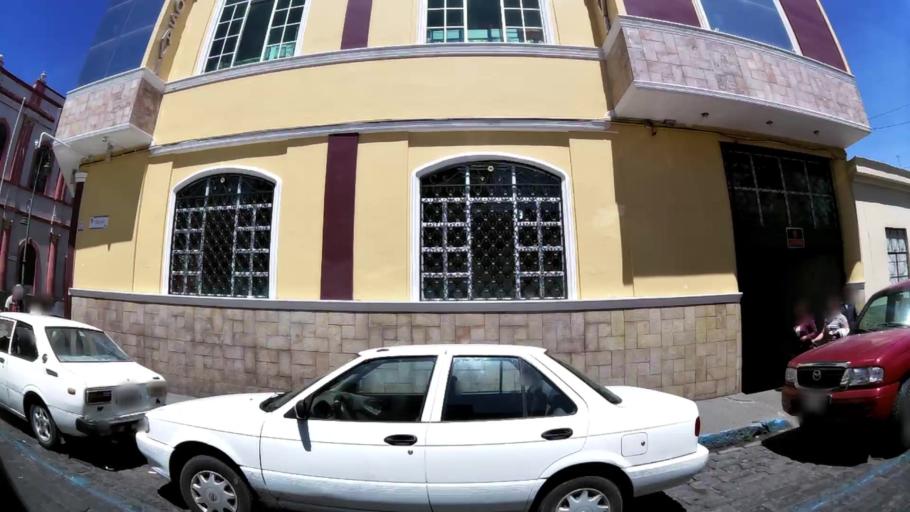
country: EC
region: Chimborazo
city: Riobamba
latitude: -1.6743
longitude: -78.6491
